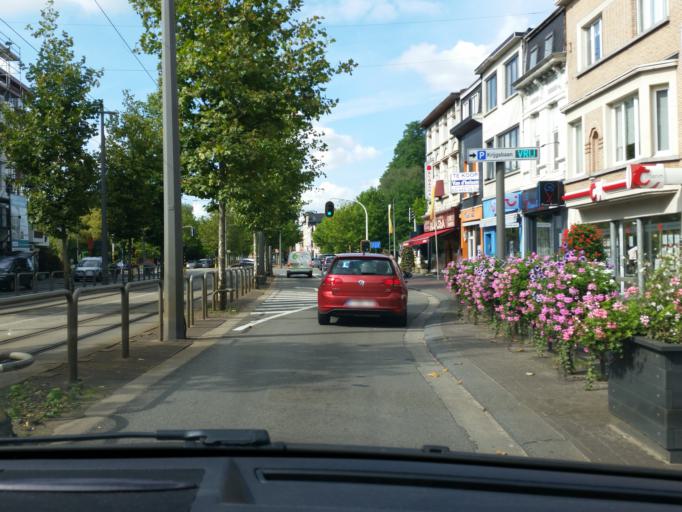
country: BE
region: Flanders
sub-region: Provincie Antwerpen
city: Mortsel
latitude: 51.1722
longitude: 4.4469
